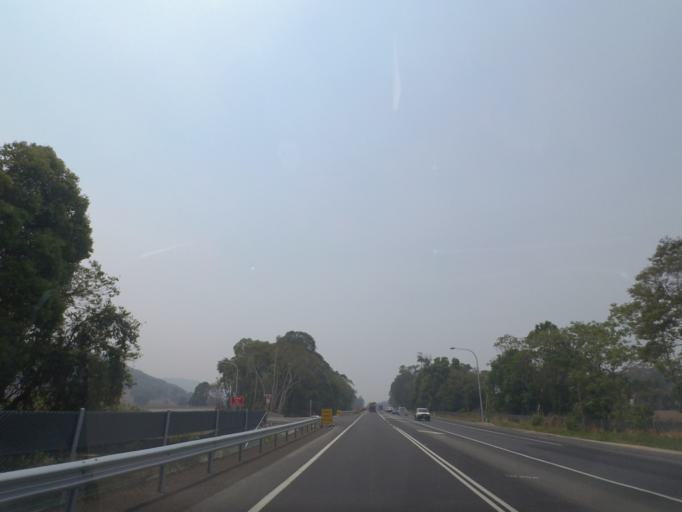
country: AU
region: New South Wales
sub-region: Ballina
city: Ballina
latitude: -28.9195
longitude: 153.4765
